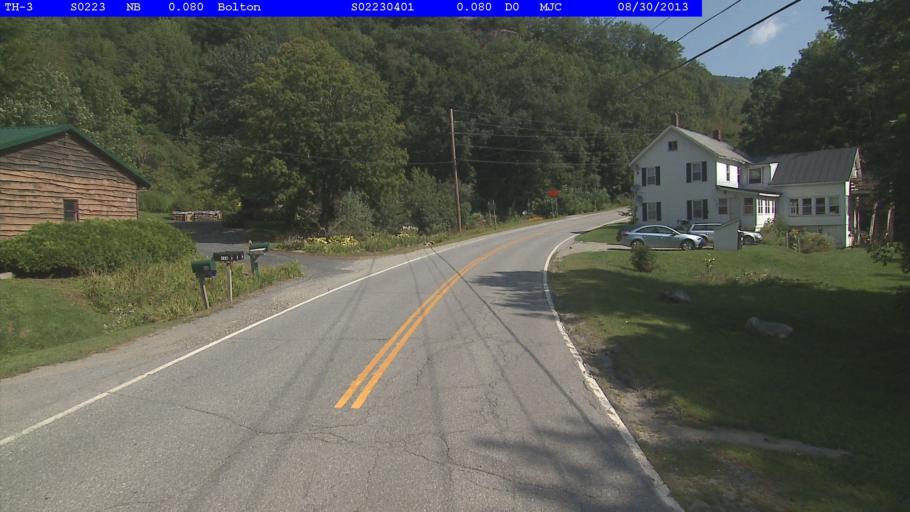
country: US
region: Vermont
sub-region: Washington County
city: Waterbury
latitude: 44.3743
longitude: -72.8785
